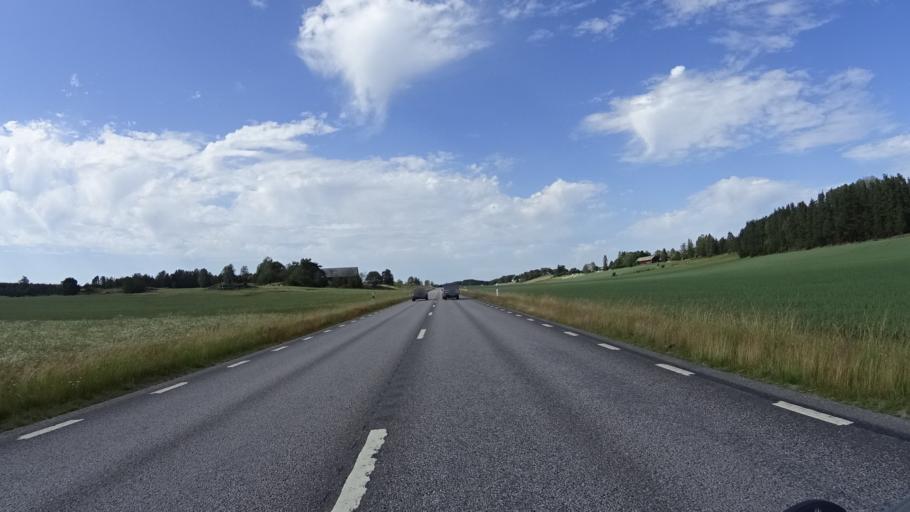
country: SE
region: OEstergoetland
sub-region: Linkopings Kommun
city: Sturefors
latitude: 58.3370
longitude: 15.8488
